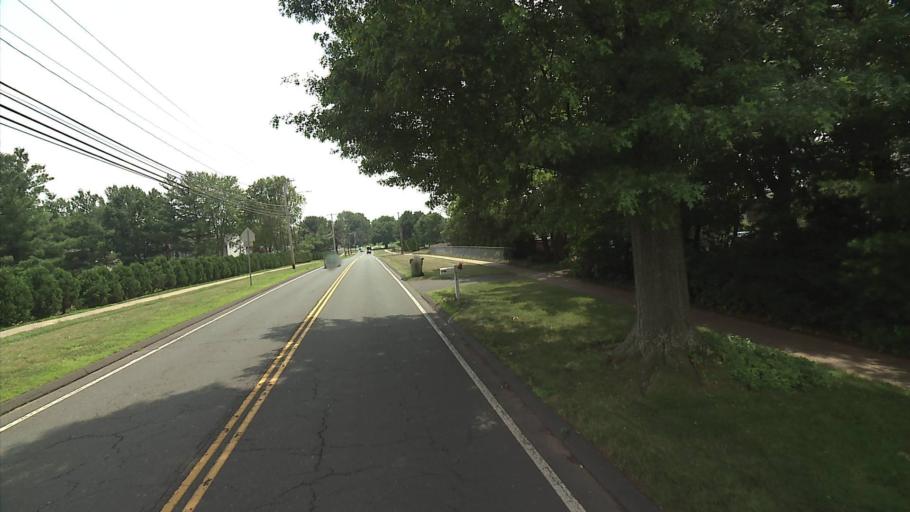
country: US
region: Connecticut
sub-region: Hartford County
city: Newington
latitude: 41.6646
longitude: -72.7272
